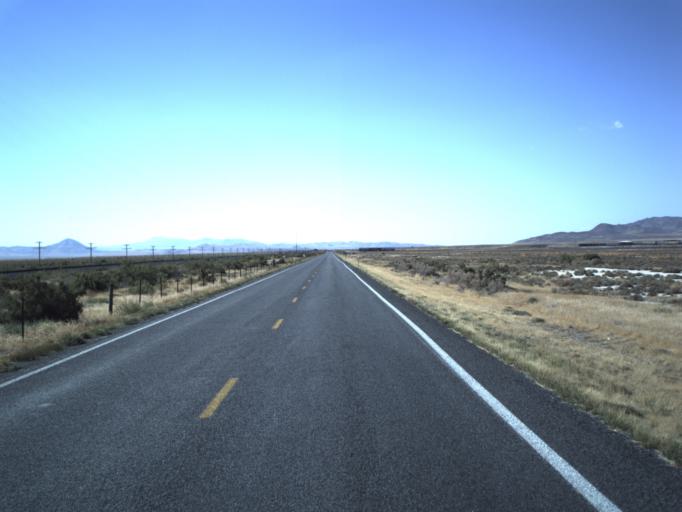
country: US
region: Utah
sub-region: Millard County
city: Delta
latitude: 38.9494
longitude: -112.8063
